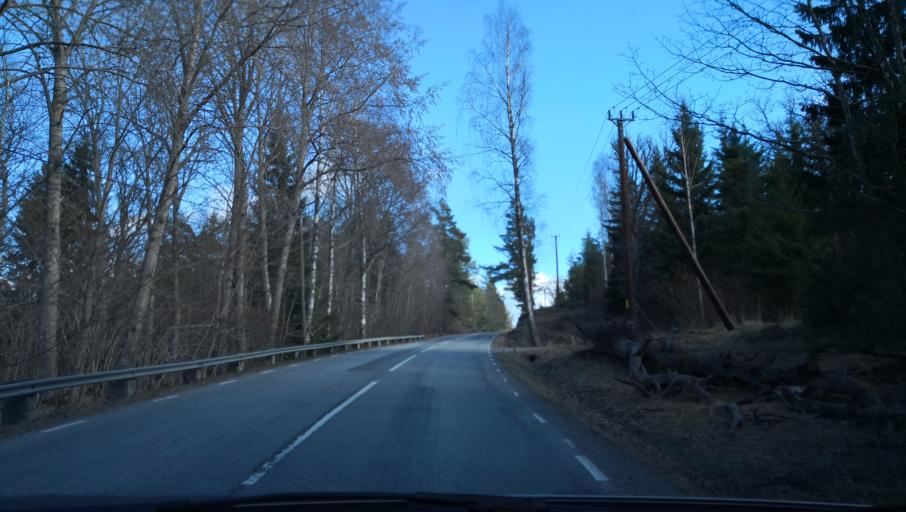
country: SE
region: Stockholm
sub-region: Varmdo Kommun
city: Hemmesta
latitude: 59.3595
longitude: 18.5464
